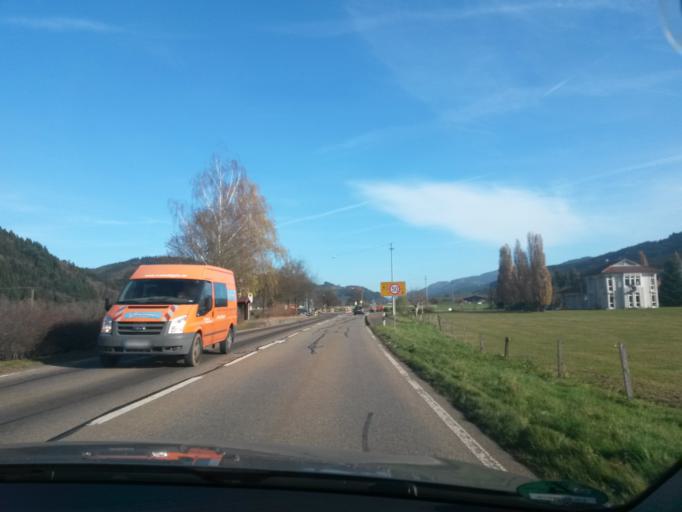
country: DE
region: Baden-Wuerttemberg
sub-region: Freiburg Region
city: Gutach im Breisgau
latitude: 48.1273
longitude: 8.0003
